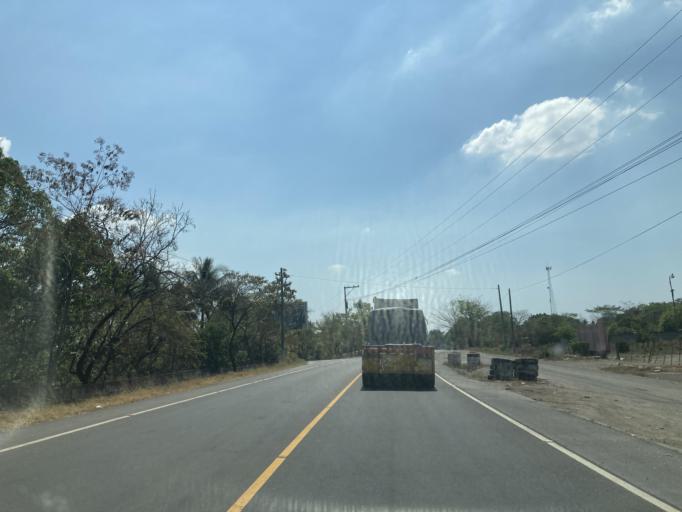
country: GT
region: Escuintla
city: Guanagazapa
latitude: 14.2057
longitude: -90.7156
